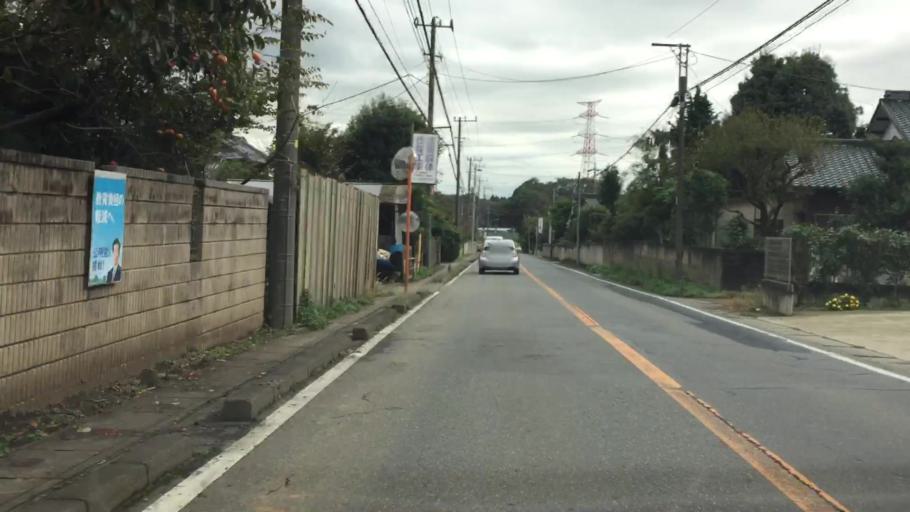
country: JP
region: Chiba
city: Abiko
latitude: 35.8428
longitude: 140.0280
